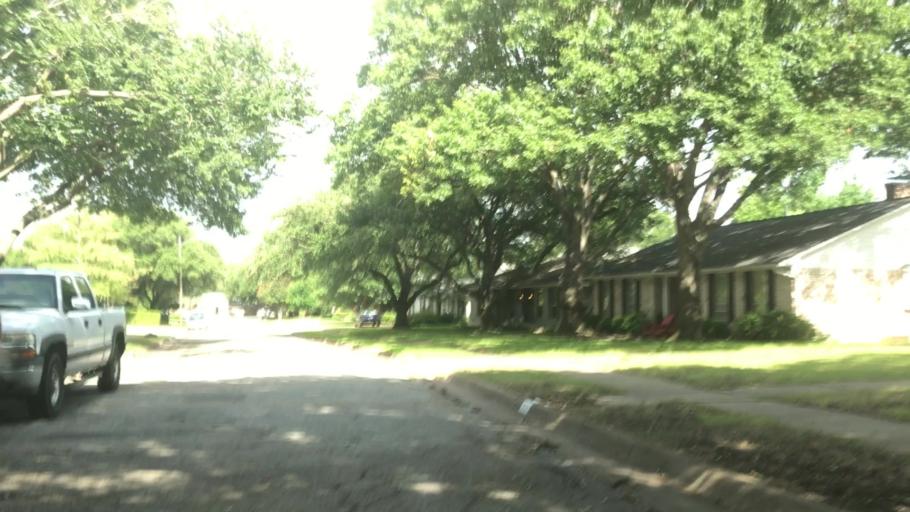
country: US
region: Texas
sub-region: Dallas County
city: Highland Park
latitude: 32.8536
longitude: -96.7549
